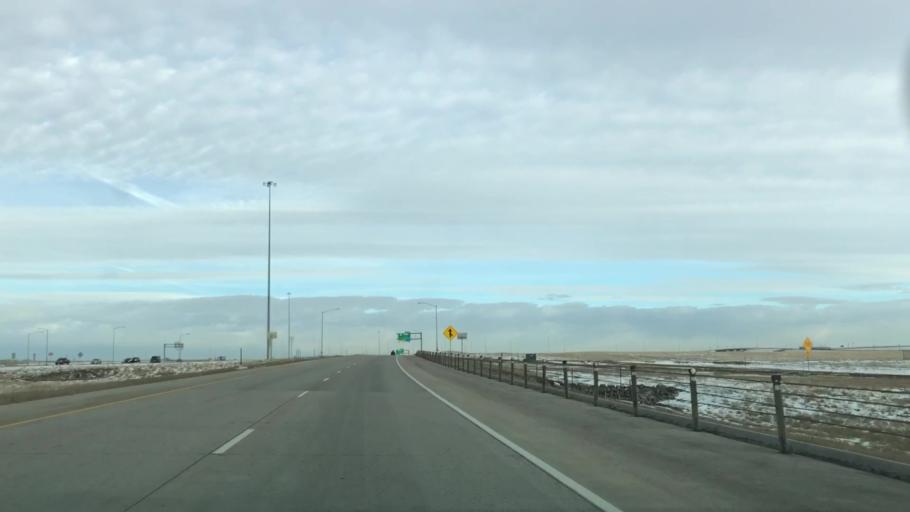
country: US
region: Colorado
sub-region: Adams County
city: Aurora
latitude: 39.8340
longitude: -104.7669
